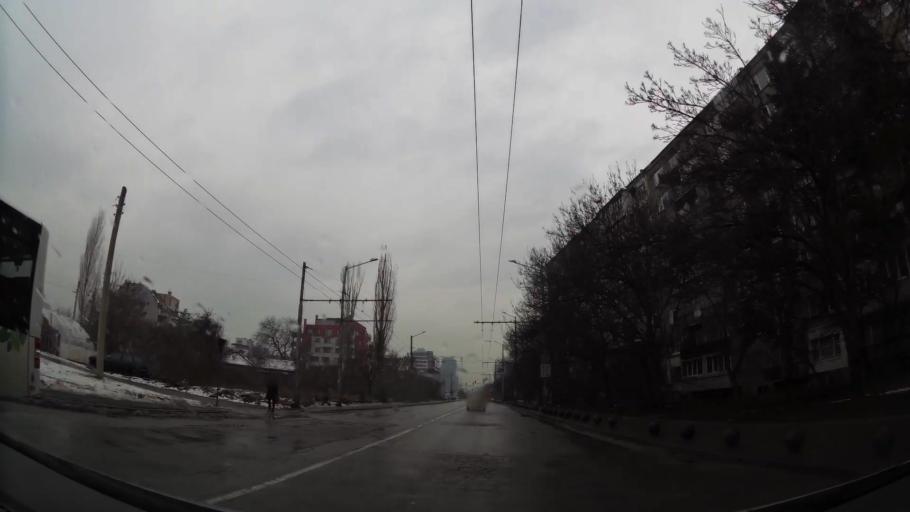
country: BG
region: Sofia-Capital
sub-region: Stolichna Obshtina
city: Sofia
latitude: 42.6607
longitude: 23.2970
